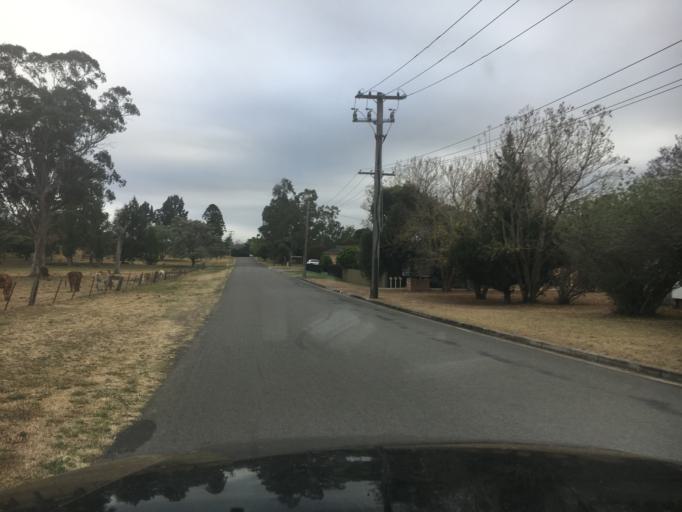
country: AU
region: New South Wales
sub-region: Singleton
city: Singleton
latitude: -32.5696
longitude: 151.1869
